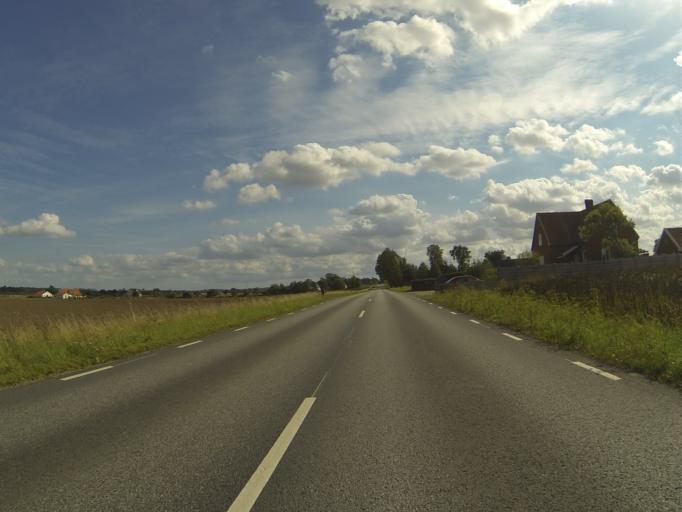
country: SE
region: Skane
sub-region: Eslovs Kommun
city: Eslov
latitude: 55.7435
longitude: 13.3277
